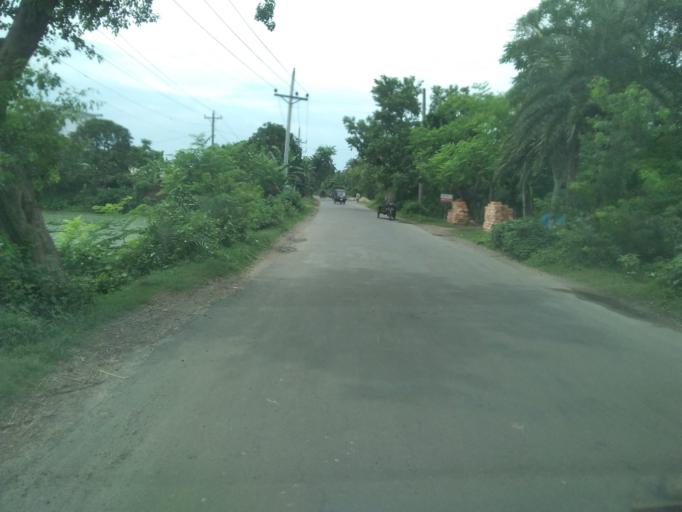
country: IN
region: West Bengal
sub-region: North 24 Parganas
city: Taki
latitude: 22.5796
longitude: 88.9983
